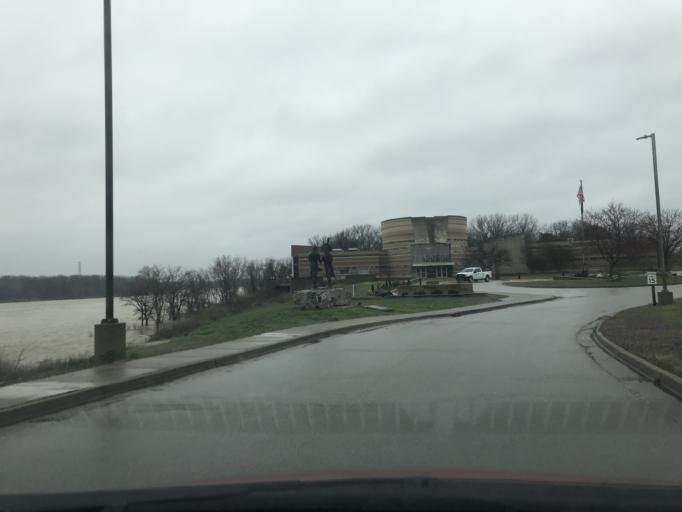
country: US
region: Indiana
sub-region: Clark County
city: Clarksville
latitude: 38.2757
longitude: -85.7629
